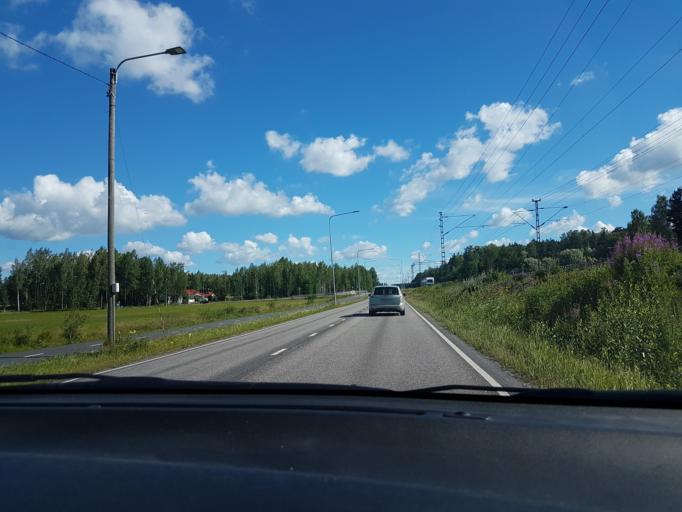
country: FI
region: Uusimaa
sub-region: Helsinki
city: Kerava
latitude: 60.3626
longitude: 25.0856
